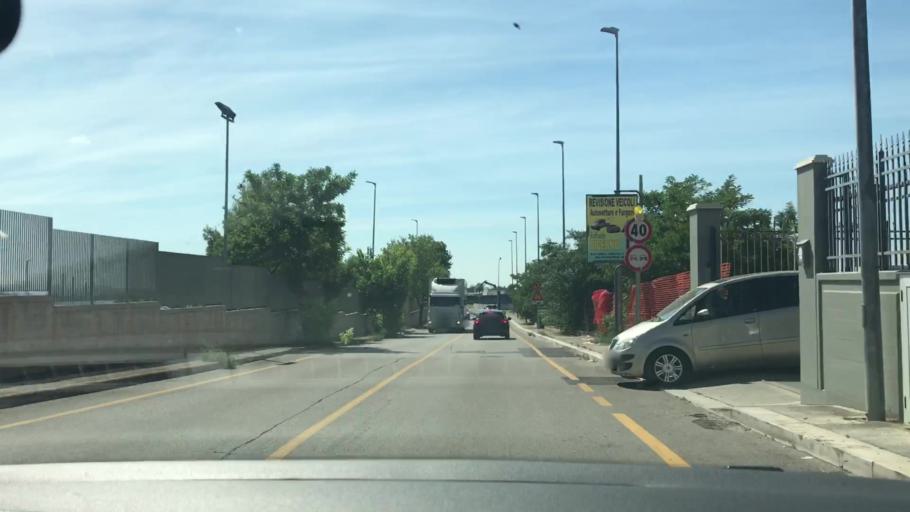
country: IT
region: Apulia
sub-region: Provincia di Bari
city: Altamura
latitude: 40.8132
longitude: 16.5538
